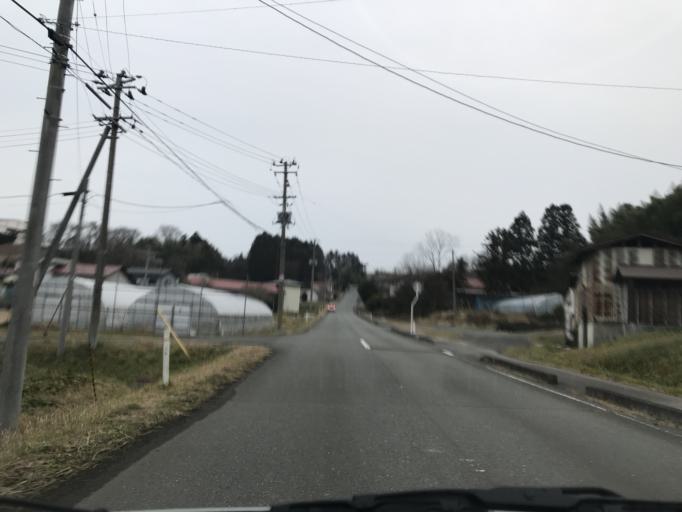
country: JP
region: Miyagi
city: Wakuya
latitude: 38.7032
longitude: 141.1575
